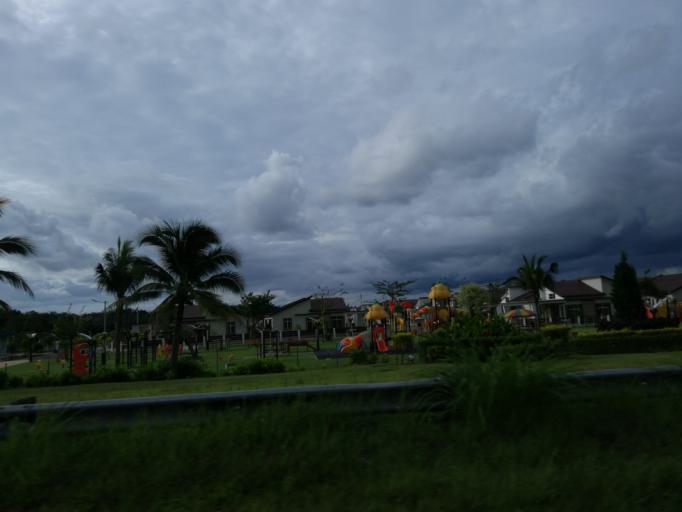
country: MY
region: Penang
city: Tasek Glugor
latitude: 5.5045
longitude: 100.6196
